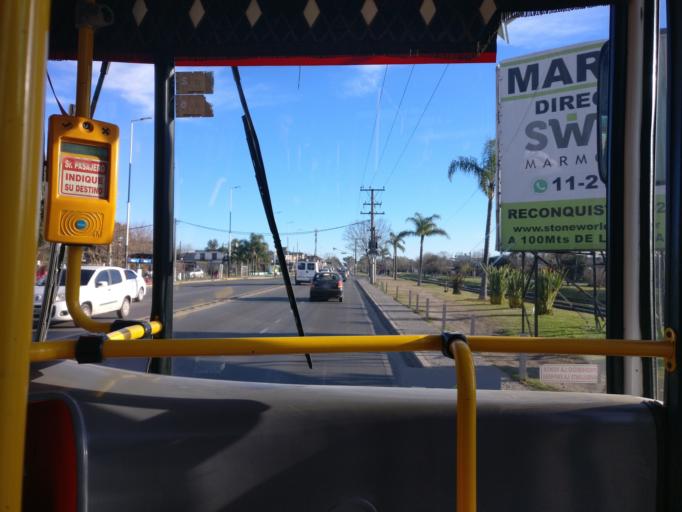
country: AR
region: Buenos Aires
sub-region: Partido de Ezeiza
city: Ezeiza
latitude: -34.8641
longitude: -58.5352
